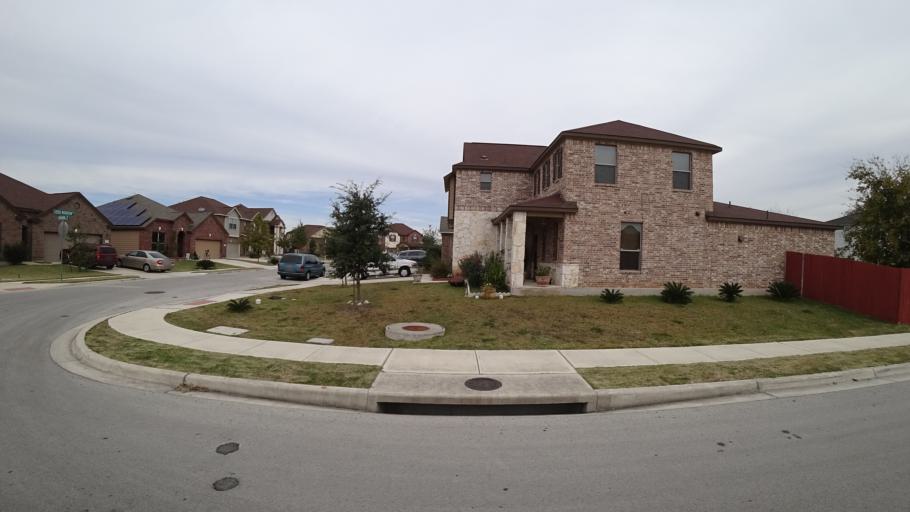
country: US
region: Texas
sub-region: Travis County
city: Onion Creek
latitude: 30.1536
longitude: -97.7437
